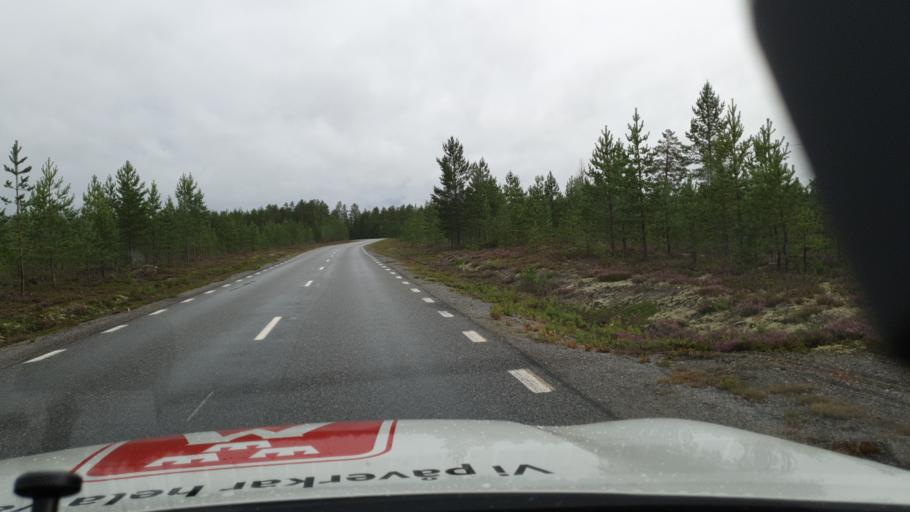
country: SE
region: Vaesterbotten
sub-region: Umea Kommun
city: Saevar
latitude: 63.9788
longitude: 20.5054
